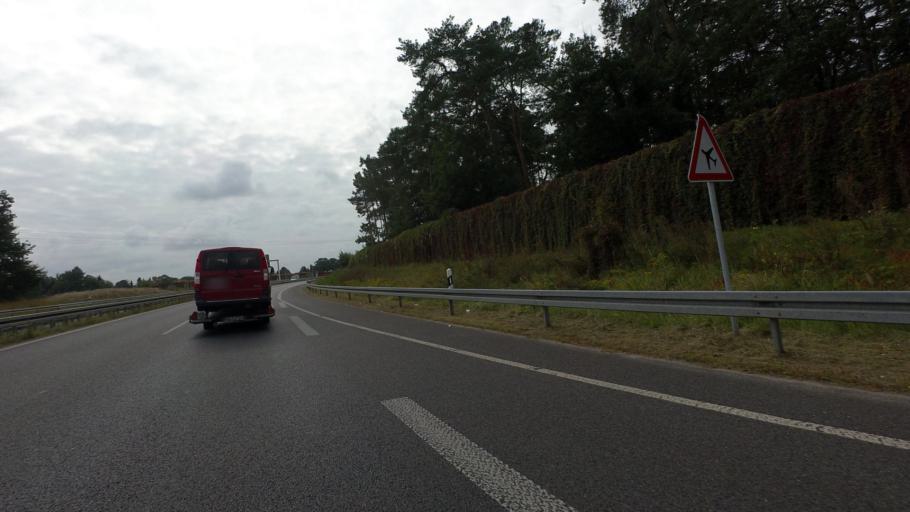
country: DE
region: Brandenburg
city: Rangsdorf
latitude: 52.3455
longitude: 13.4457
